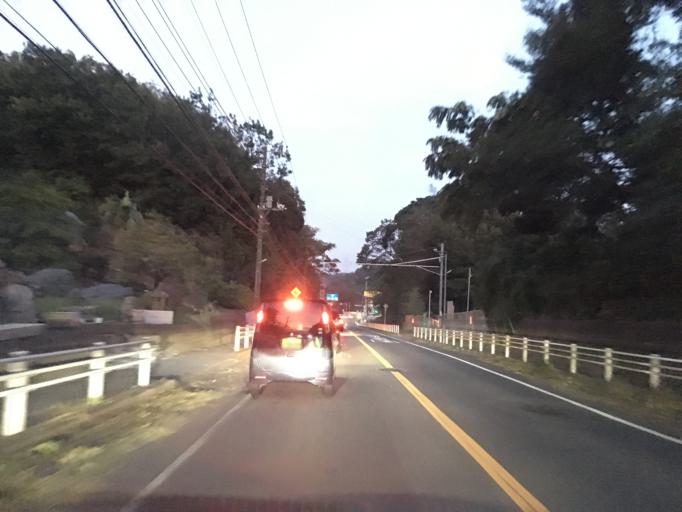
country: JP
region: Chiba
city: Kisarazu
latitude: 35.3446
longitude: 139.9186
